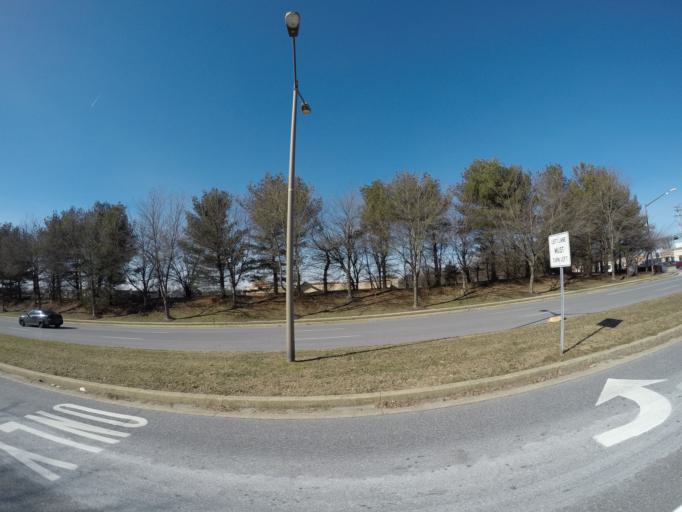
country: US
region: Maryland
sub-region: Howard County
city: Ellicott City
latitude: 39.2506
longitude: -76.8140
